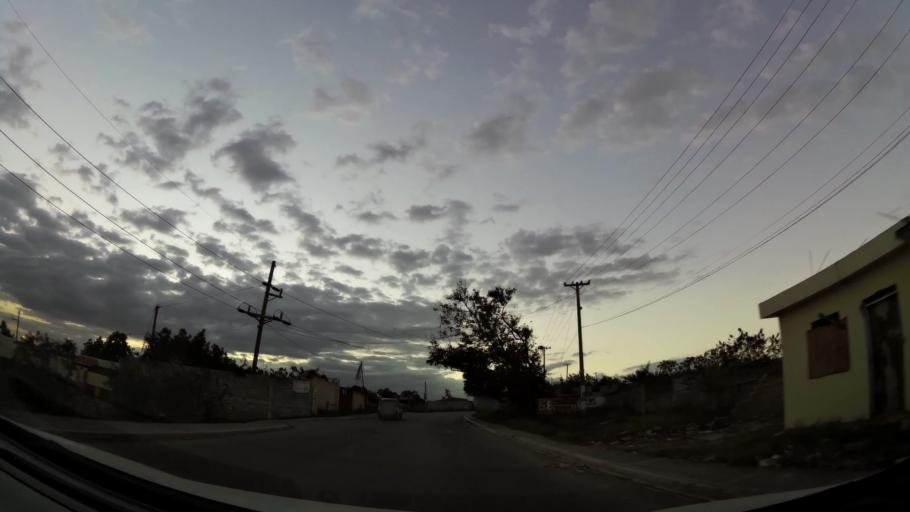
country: DO
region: Nacional
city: La Agustina
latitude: 18.5546
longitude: -69.9473
